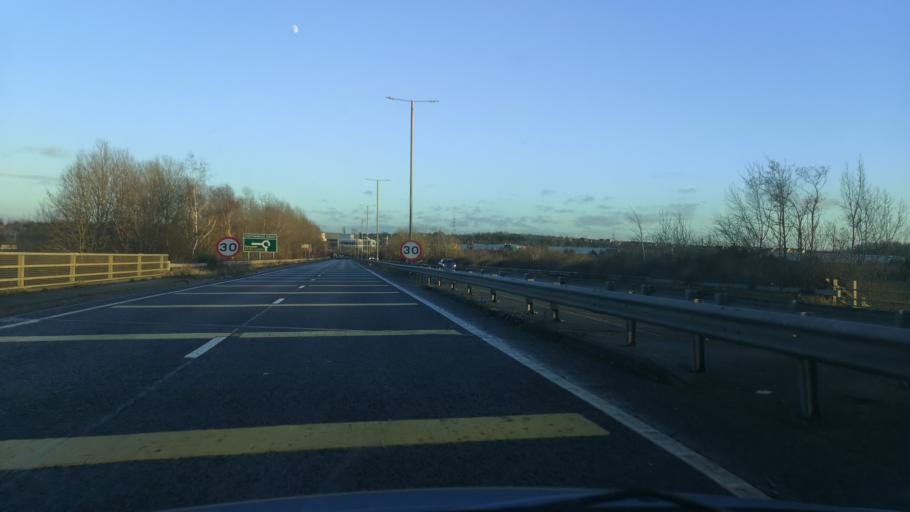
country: GB
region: England
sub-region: Barnsley
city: Wombwell
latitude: 53.5106
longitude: -1.3961
